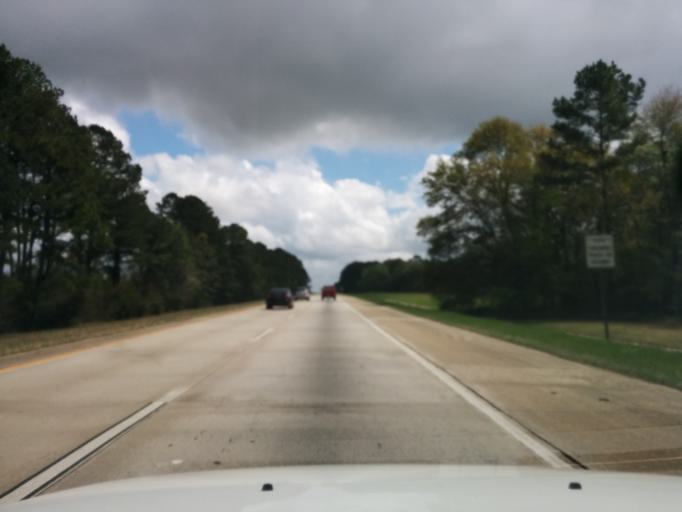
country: US
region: Georgia
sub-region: Bulloch County
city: Statesboro
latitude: 32.2900
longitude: -81.8044
